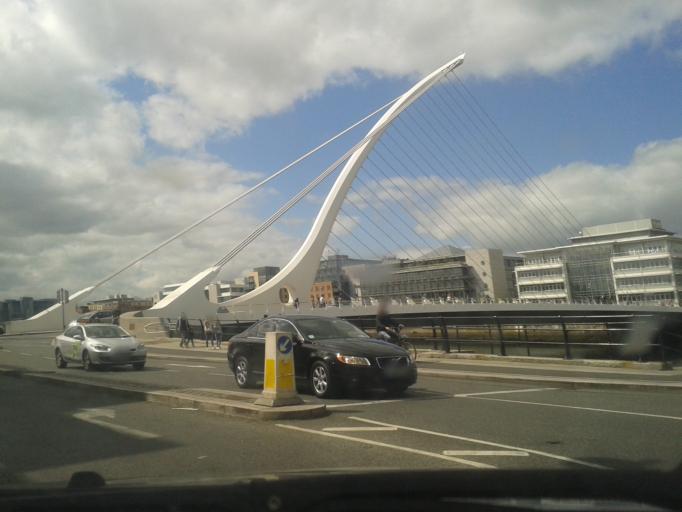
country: IE
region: Leinster
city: Ringsend
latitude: 53.3460
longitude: -6.2404
